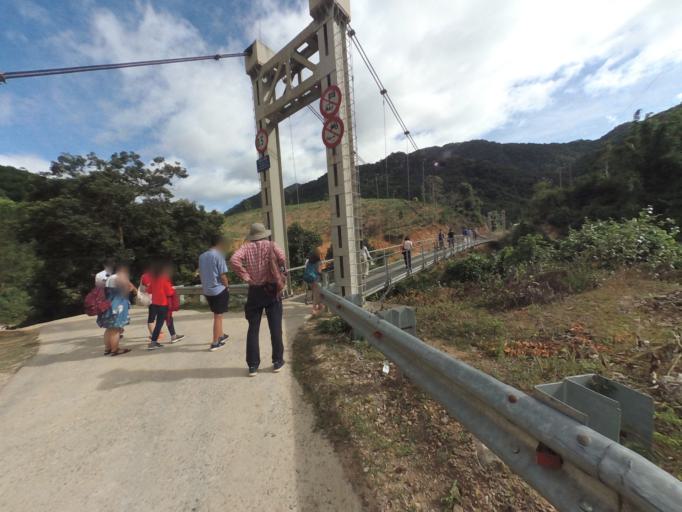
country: VN
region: Thua Thien-Hue
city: A Luoi
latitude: 16.3043
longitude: 107.2137
